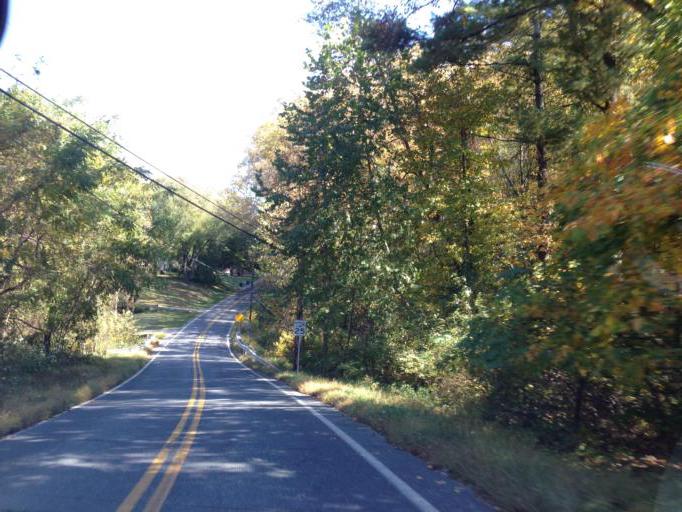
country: US
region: Maryland
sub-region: Howard County
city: North Laurel
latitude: 39.1333
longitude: -76.8965
